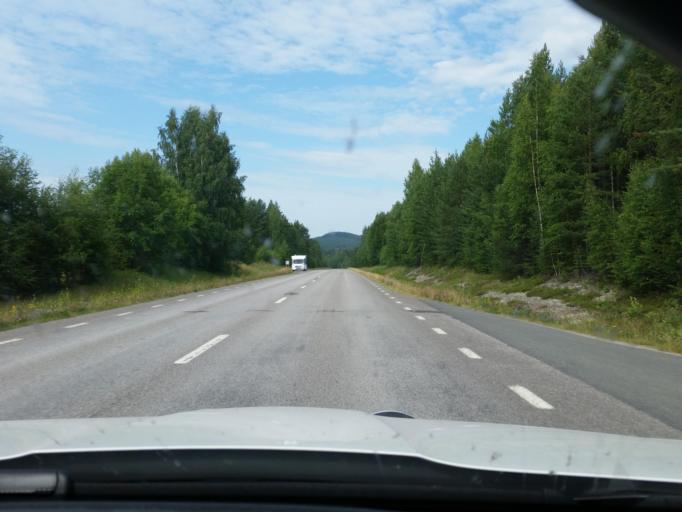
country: SE
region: Norrbotten
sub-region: Alvsbyns Kommun
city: AElvsbyn
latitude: 65.6795
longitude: 20.8133
